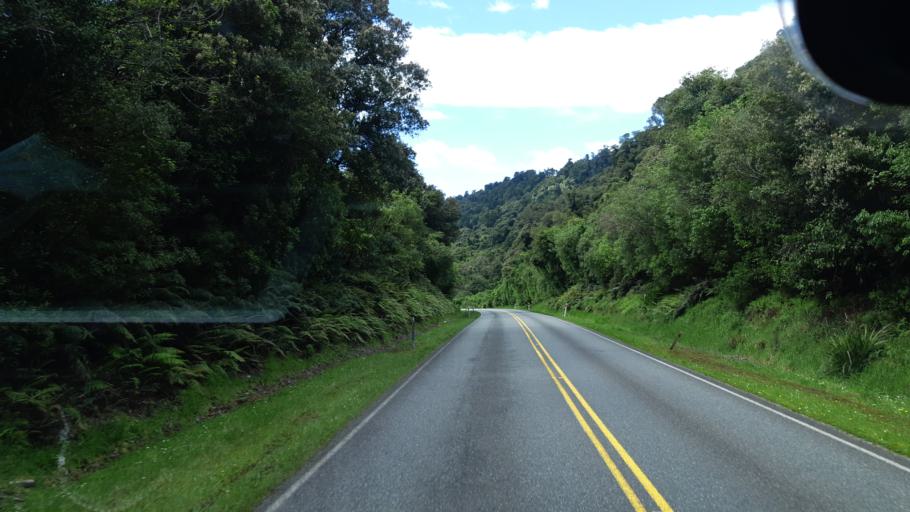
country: NZ
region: West Coast
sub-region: Westland District
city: Hokitika
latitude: -43.0678
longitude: 170.6286
